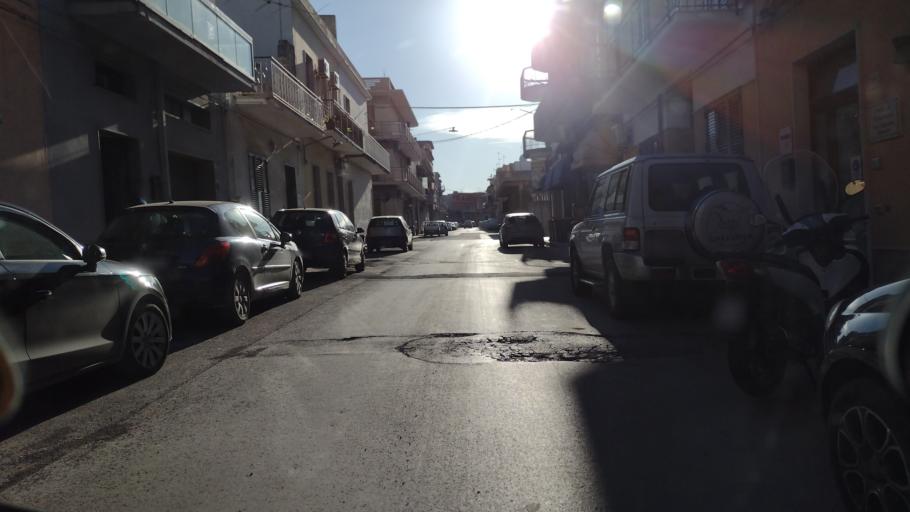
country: IT
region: Sicily
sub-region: Provincia di Siracusa
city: Avola
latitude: 36.9026
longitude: 15.1380
